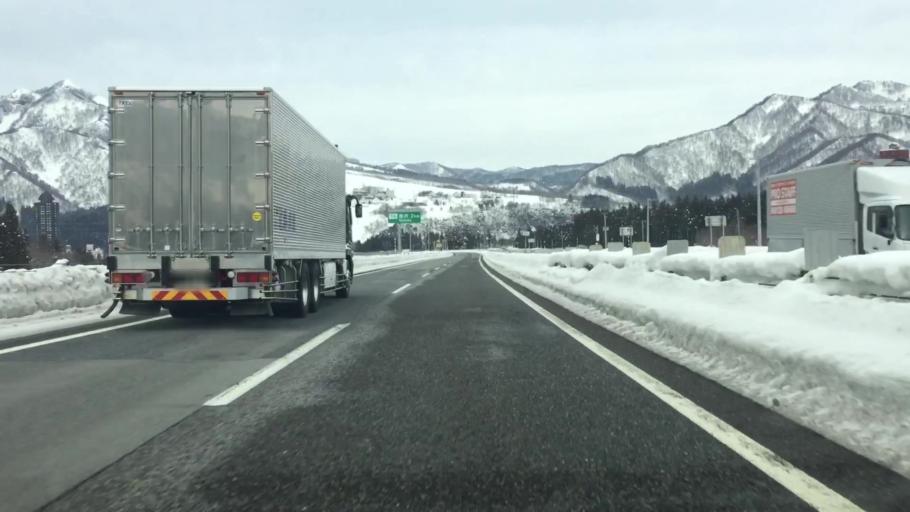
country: JP
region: Niigata
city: Shiozawa
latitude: 36.9189
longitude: 138.8403
